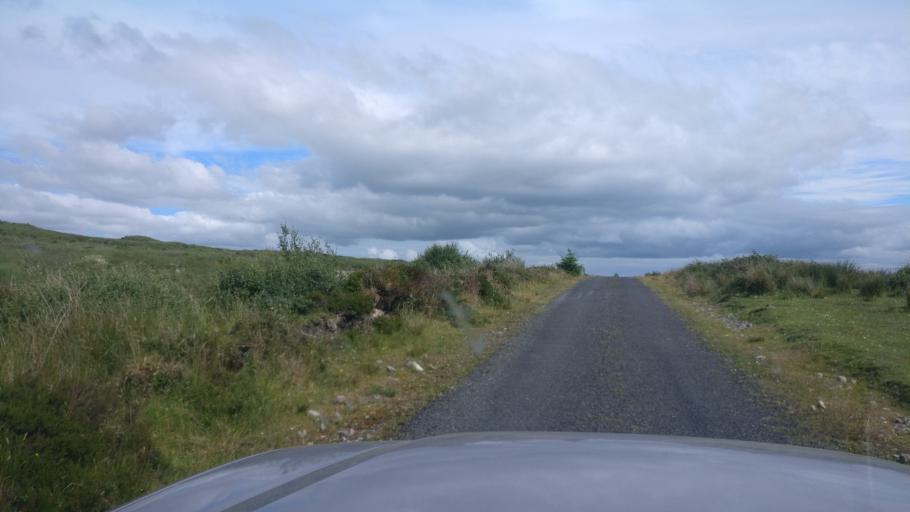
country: IE
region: Connaught
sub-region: County Galway
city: Gort
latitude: 53.0811
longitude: -8.6872
